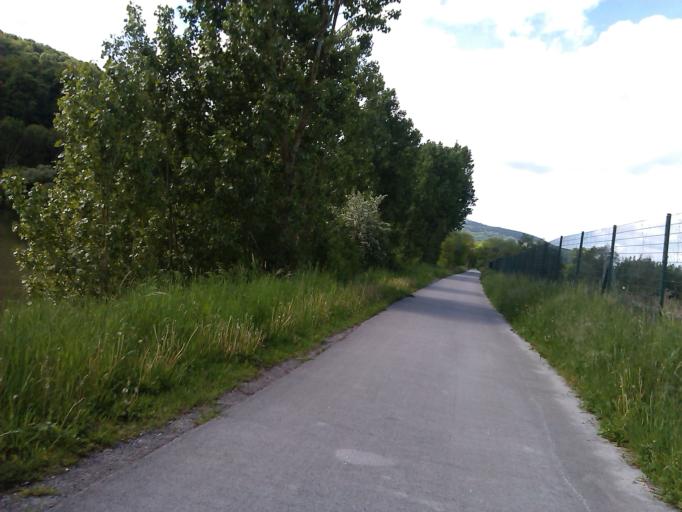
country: FR
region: Franche-Comte
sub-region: Departement du Doubs
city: Novillars
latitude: 47.2841
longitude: 6.1387
